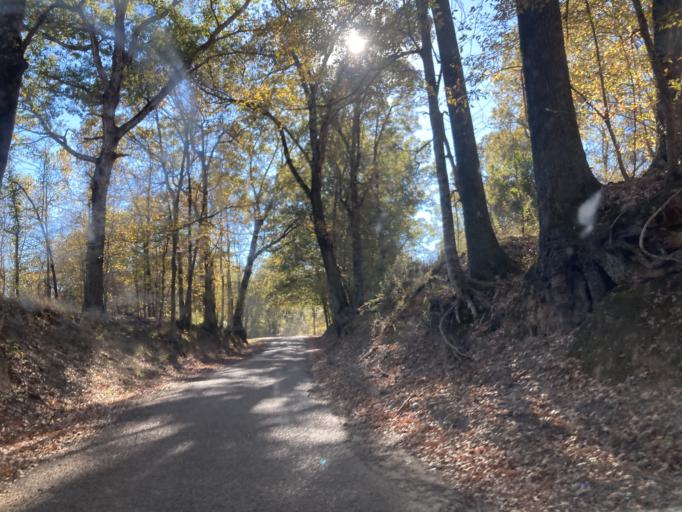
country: US
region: Mississippi
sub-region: Yazoo County
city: Yazoo City
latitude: 32.7782
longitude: -90.4071
